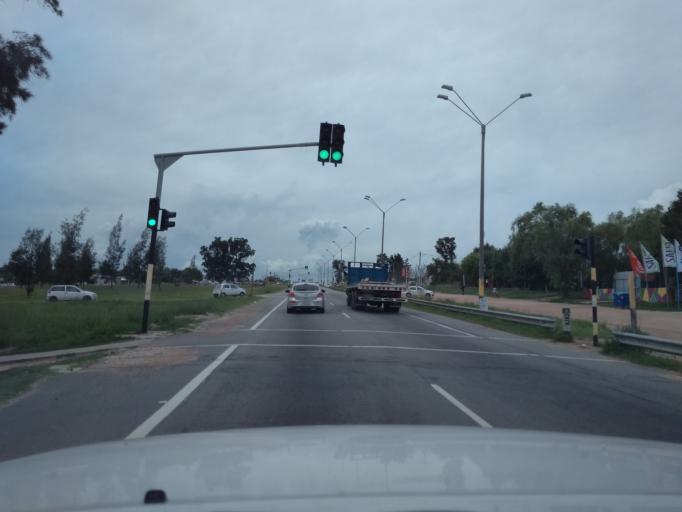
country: UY
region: Canelones
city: Colonia Nicolich
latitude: -34.8210
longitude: -56.0088
